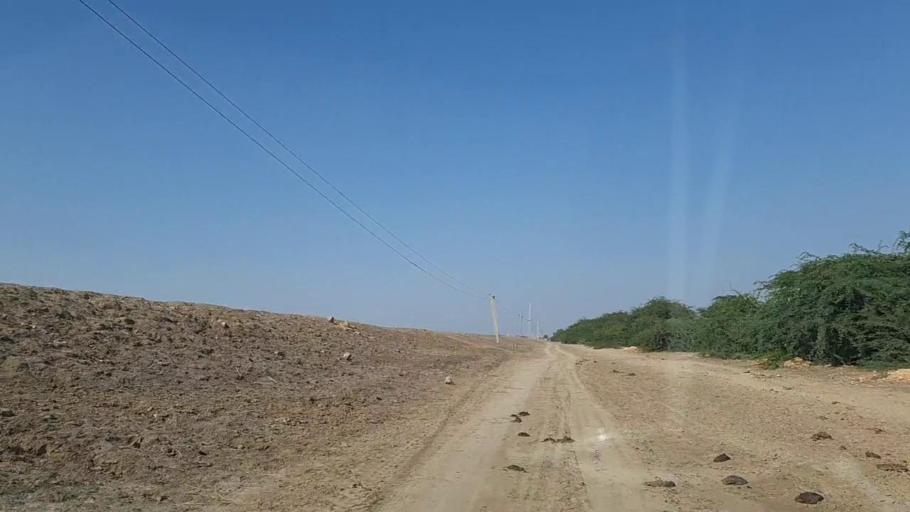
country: PK
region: Sindh
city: Chuhar Jamali
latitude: 24.5389
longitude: 68.0158
